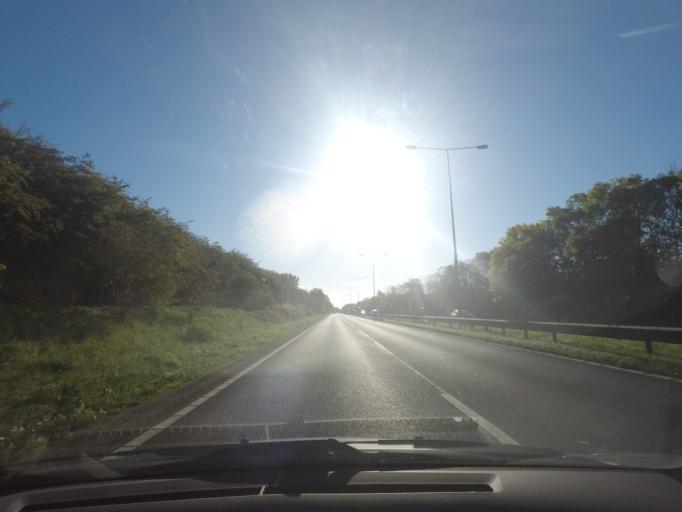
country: GB
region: England
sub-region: East Riding of Yorkshire
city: Brantingham
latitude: 53.7503
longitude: -0.5774
